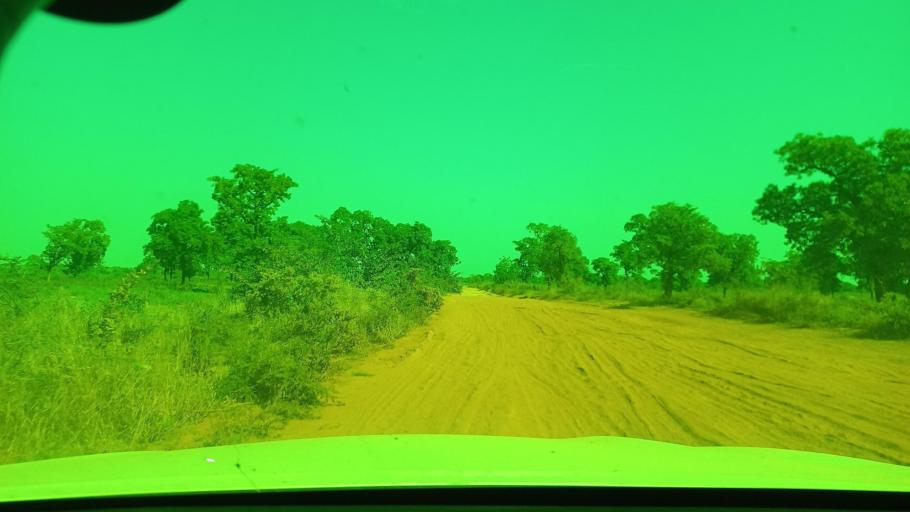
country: ML
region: Bamako
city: Bamako
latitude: 12.3977
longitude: -7.9961
